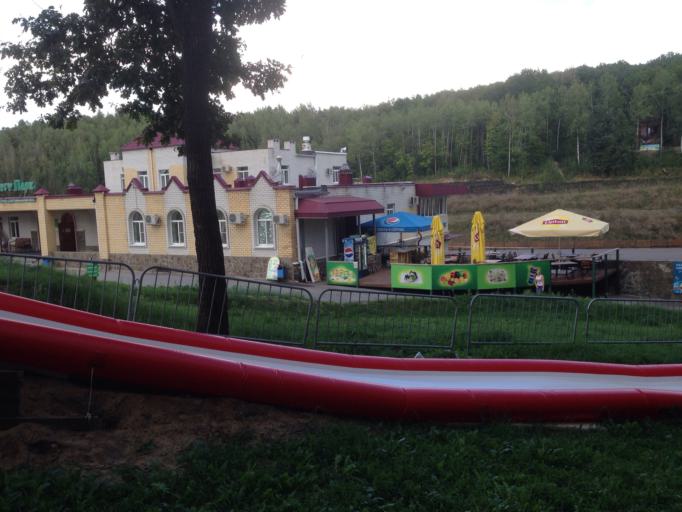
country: RU
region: Lipetsk
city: Zadonsk
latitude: 52.3631
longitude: 38.9209
